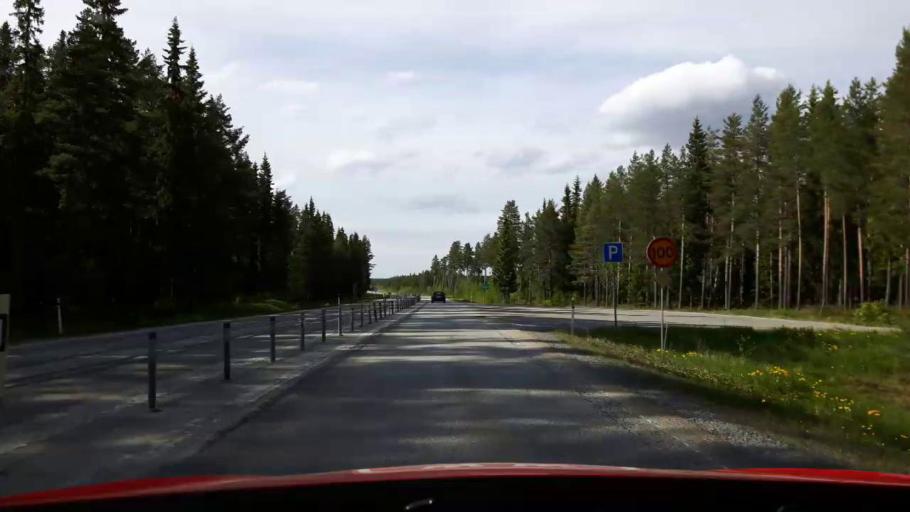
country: SE
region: Jaemtland
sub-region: OEstersunds Kommun
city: Brunflo
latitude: 63.1467
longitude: 14.7791
